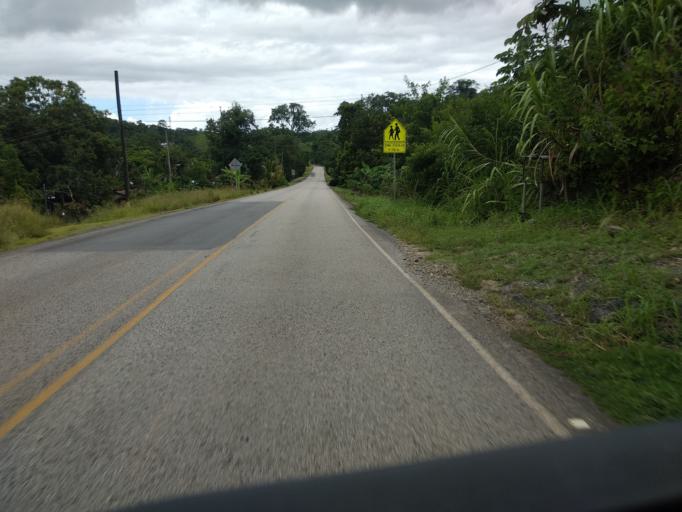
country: CR
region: Puntarenas
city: Buenos Aires
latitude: 9.1032
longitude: -83.2829
